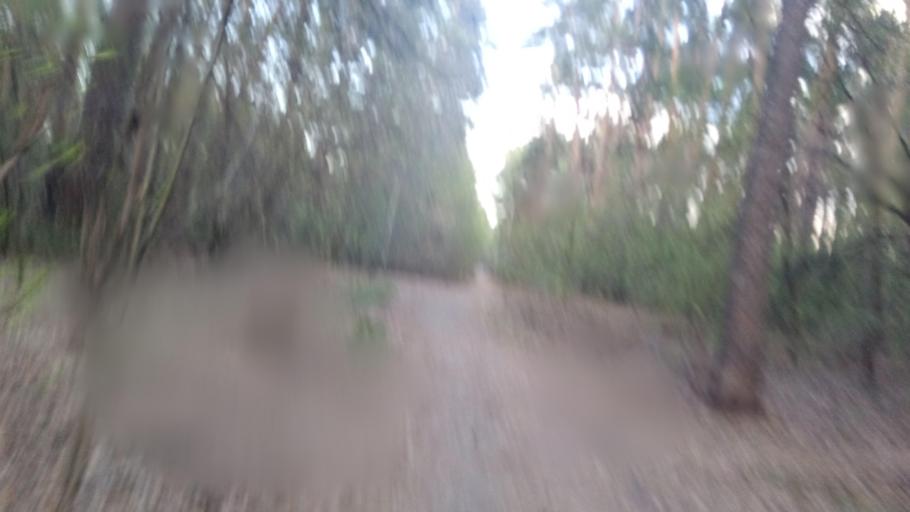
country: RU
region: Chelyabinsk
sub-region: Gorod Chelyabinsk
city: Chelyabinsk
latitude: 55.1671
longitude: 61.3473
